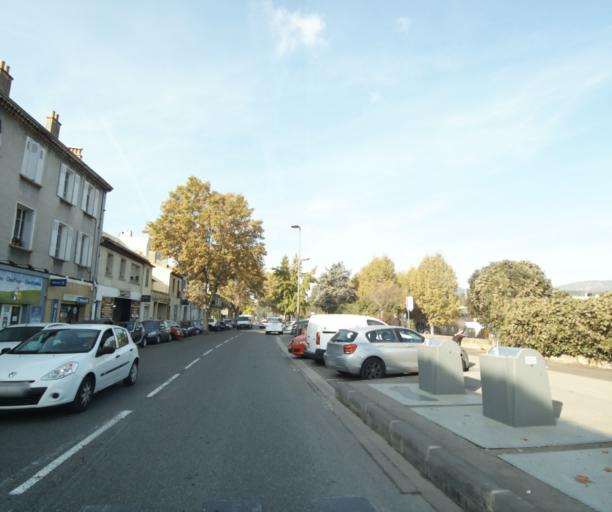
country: FR
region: Provence-Alpes-Cote d'Azur
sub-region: Departement des Bouches-du-Rhone
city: Aubagne
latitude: 43.2926
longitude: 5.5649
